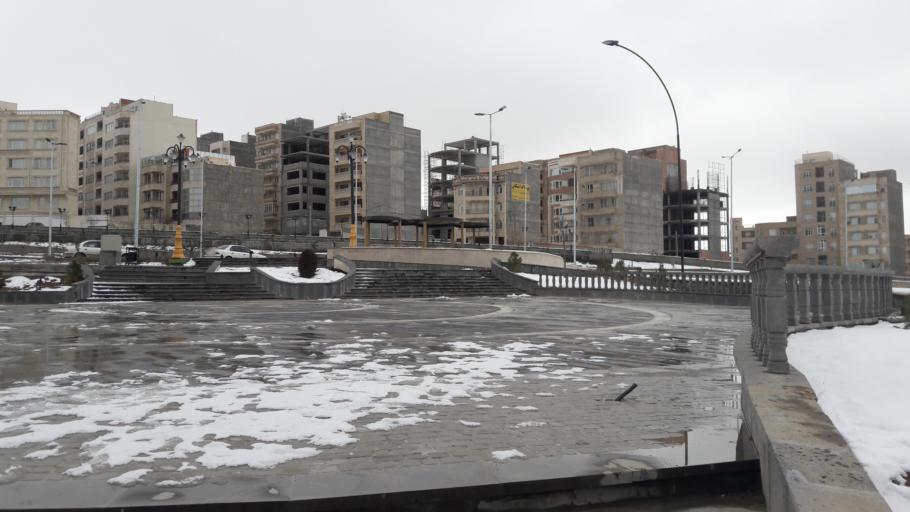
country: IR
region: Ardabil
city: Ardabil
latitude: 38.2156
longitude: 48.2716
